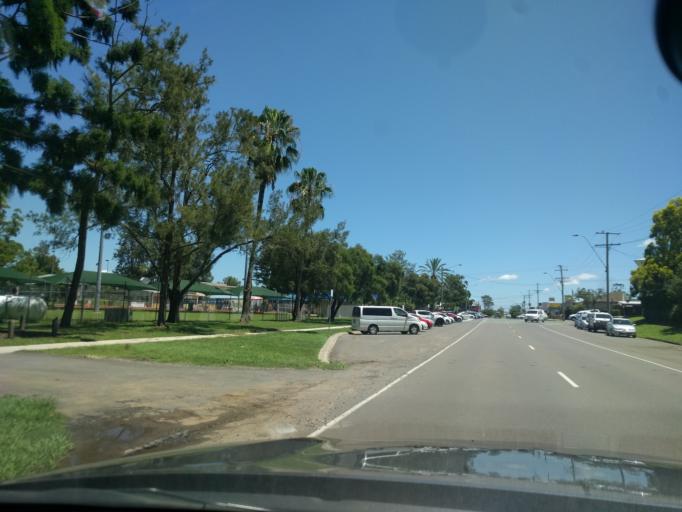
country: AU
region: Queensland
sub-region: Logan
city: Cedar Vale
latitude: -27.9915
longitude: 152.9962
